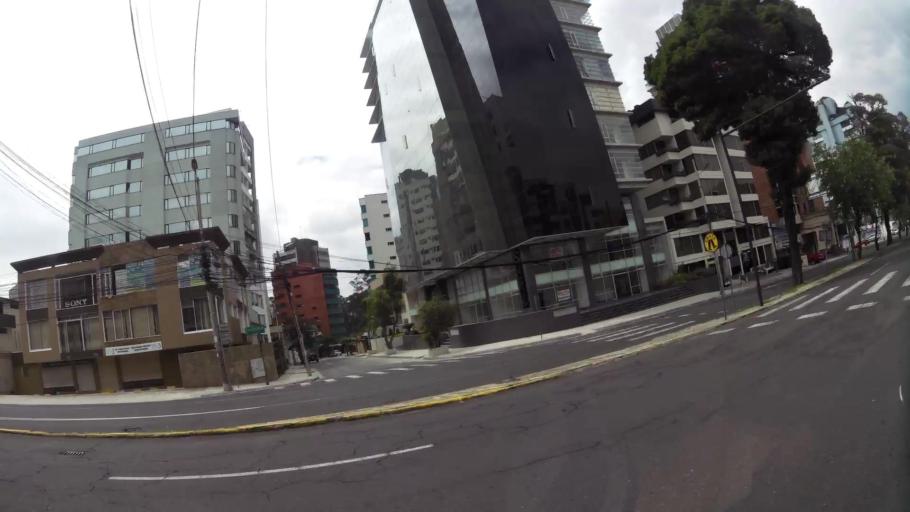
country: EC
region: Pichincha
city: Quito
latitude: -0.1851
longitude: -78.4888
